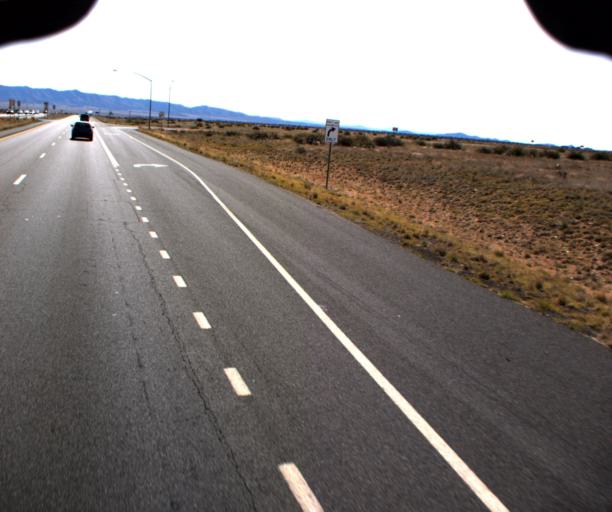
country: US
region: Arizona
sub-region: Yavapai County
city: Prescott Valley
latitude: 34.6305
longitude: -112.3770
